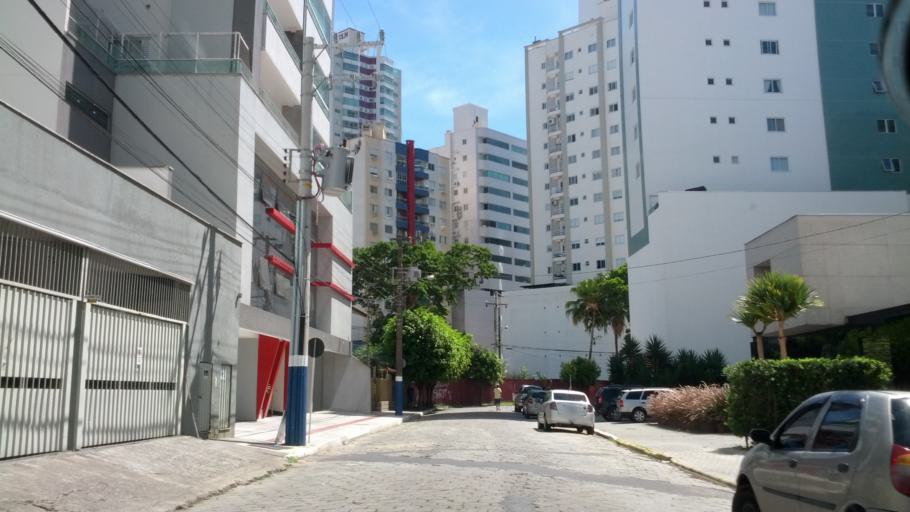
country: BR
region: Santa Catarina
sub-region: Balneario Camboriu
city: Balneario Camboriu
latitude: -27.0009
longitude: -48.6298
